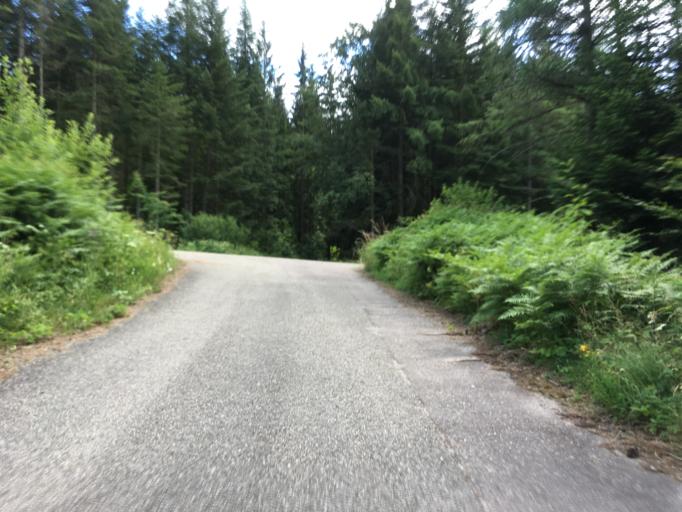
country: DE
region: Baden-Wuerttemberg
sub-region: Karlsruhe Region
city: Baiersbronn
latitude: 48.5279
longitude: 8.4281
